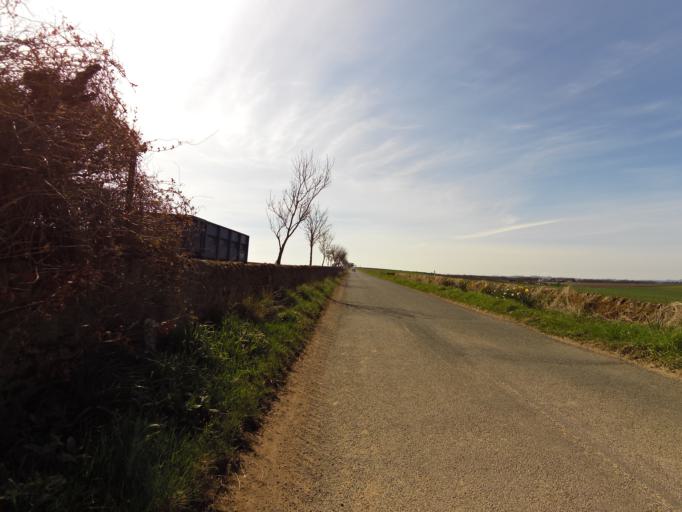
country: GB
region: Scotland
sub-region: Angus
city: Arbroath
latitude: 56.6065
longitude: -2.5234
